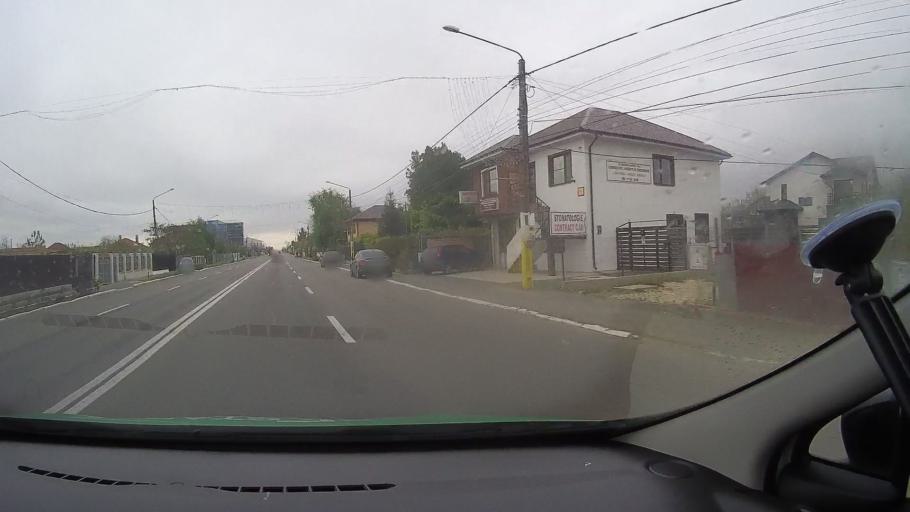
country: RO
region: Constanta
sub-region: Comuna Valu lui Traian
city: Valu lui Traian
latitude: 44.1656
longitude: 28.4660
